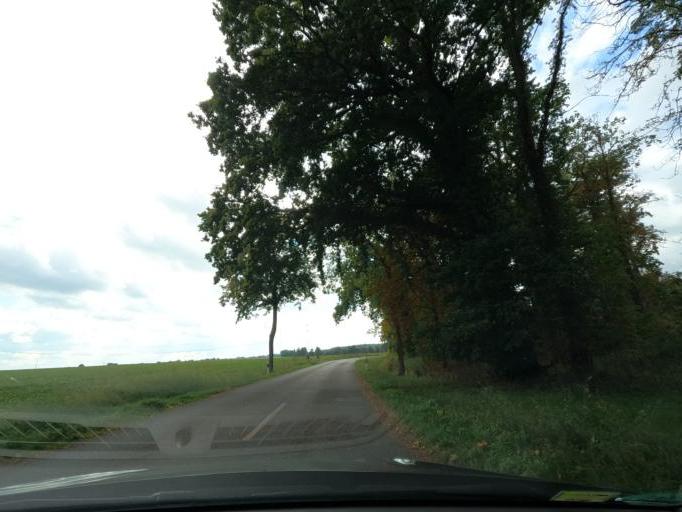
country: DE
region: Lower Saxony
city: Adenbuettel
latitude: 52.3720
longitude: 10.4367
